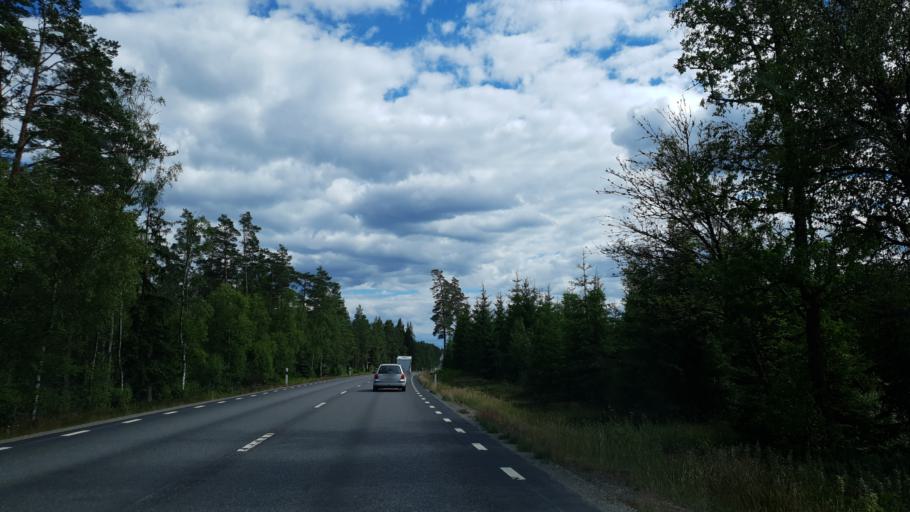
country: SE
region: Kronoberg
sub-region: Lessebo Kommun
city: Lessebo
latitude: 56.8271
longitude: 15.4017
